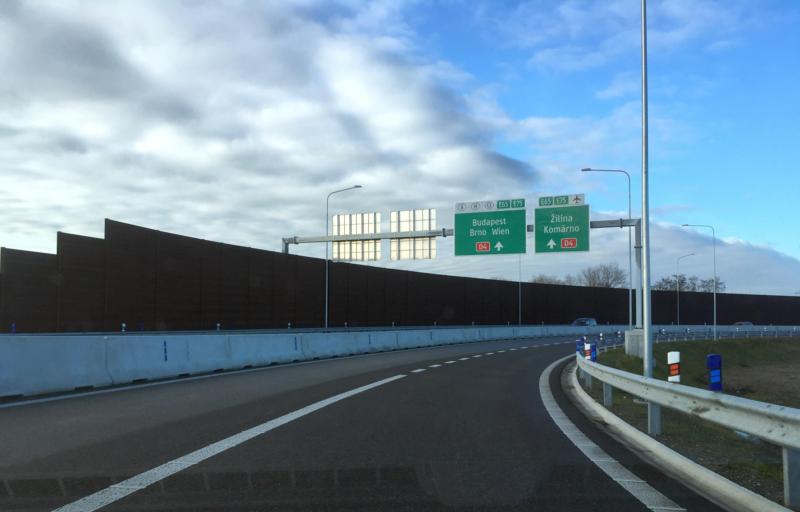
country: AT
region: Burgenland
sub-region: Politischer Bezirk Neusiedl am See
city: Deutsch Jahrndorf
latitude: 48.0743
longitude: 17.1327
